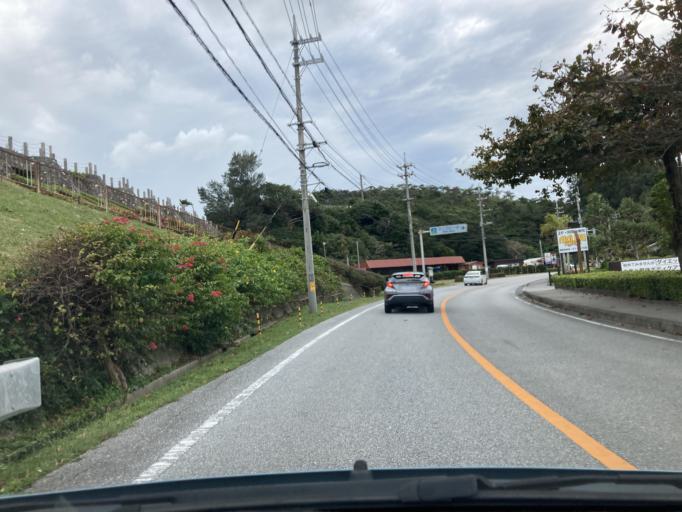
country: JP
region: Okinawa
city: Ishikawa
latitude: 26.4347
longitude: 127.7840
